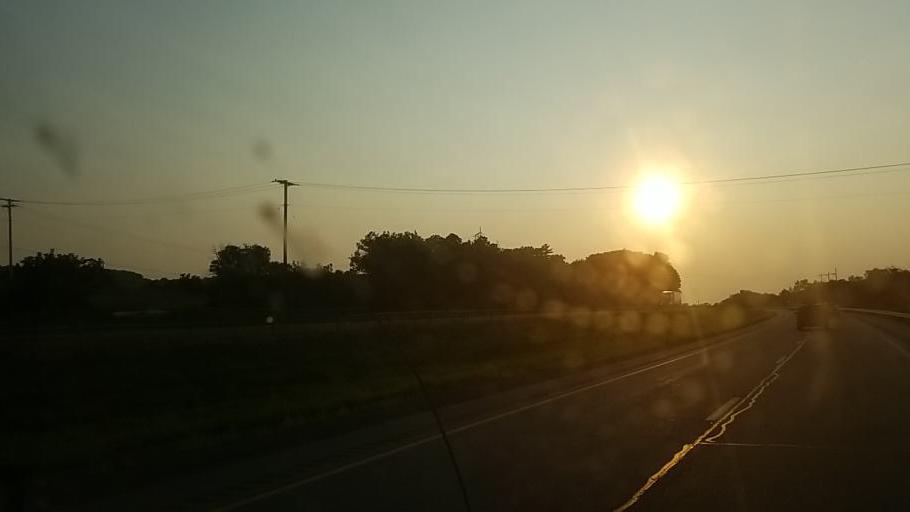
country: US
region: New York
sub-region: Montgomery County
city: Saint Johnsville
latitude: 42.9895
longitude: -74.6716
